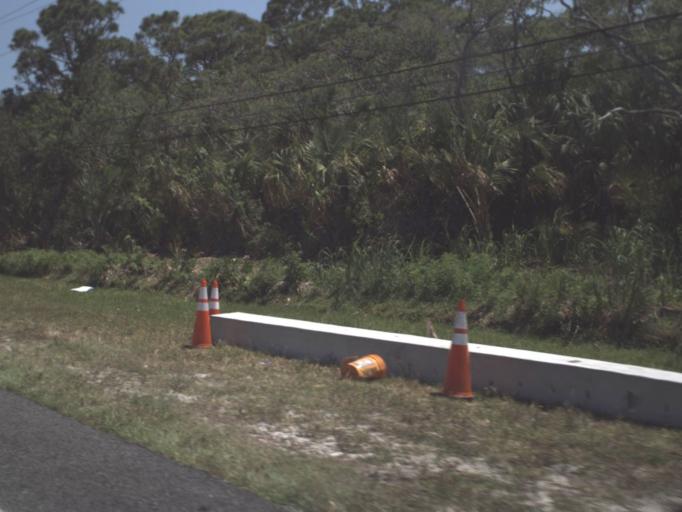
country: US
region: Florida
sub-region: Brevard County
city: Grant-Valkaria
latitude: 27.9548
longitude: -80.5377
